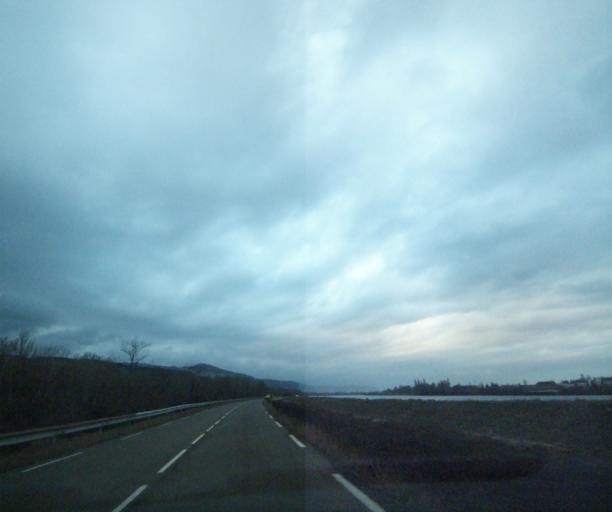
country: FR
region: Rhone-Alpes
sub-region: Departement de l'Ardeche
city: Cornas
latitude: 44.9665
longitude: 4.8627
